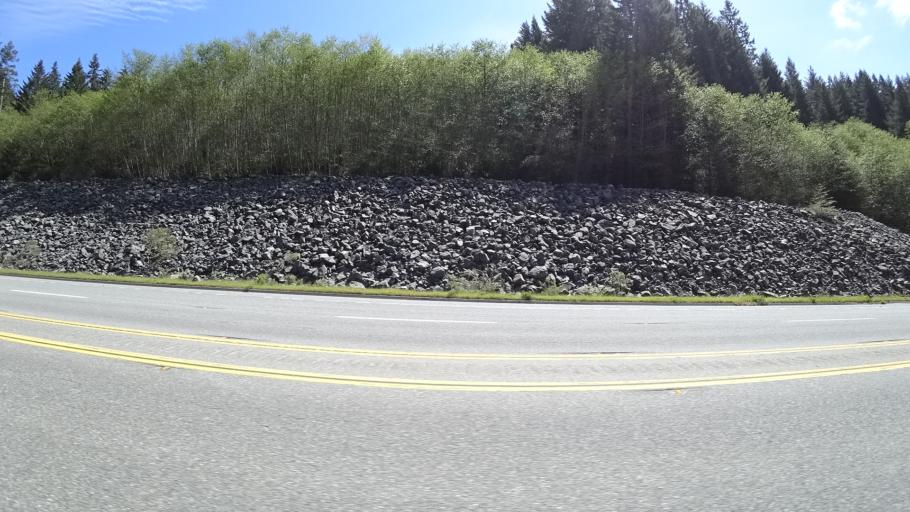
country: US
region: California
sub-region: Humboldt County
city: Westhaven-Moonstone
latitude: 41.3822
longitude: -123.9950
